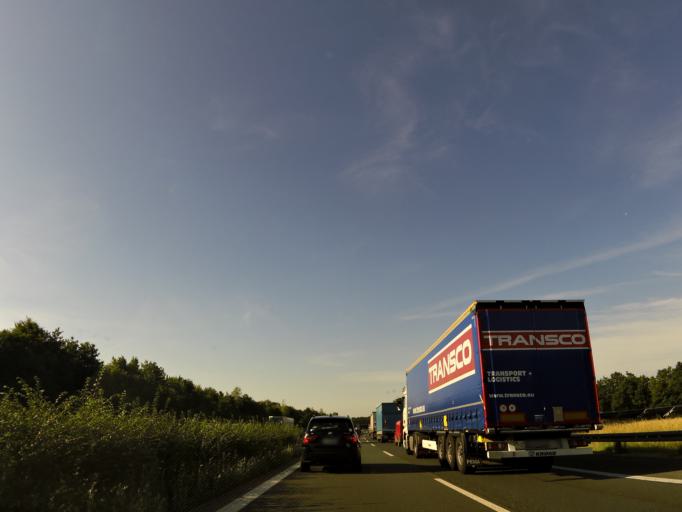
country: DE
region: Bavaria
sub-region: Regierungsbezirk Mittelfranken
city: Hessdorf
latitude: 49.6049
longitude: 10.9277
